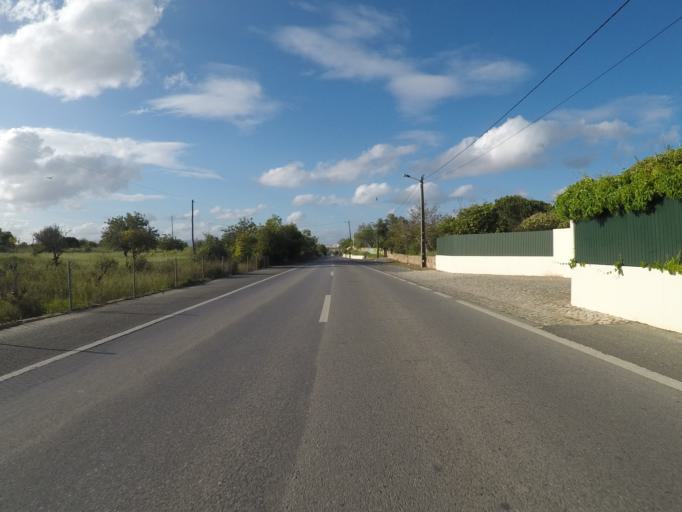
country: PT
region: Faro
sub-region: Lagoa
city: Lagoa
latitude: 37.1214
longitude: -8.4543
